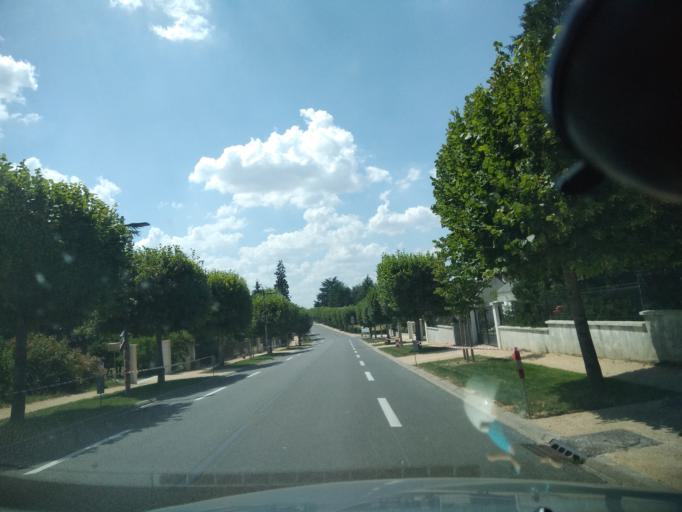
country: FR
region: Centre
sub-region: Departement d'Indre-et-Loire
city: Civray-de-Touraine
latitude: 47.3319
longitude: 1.0760
